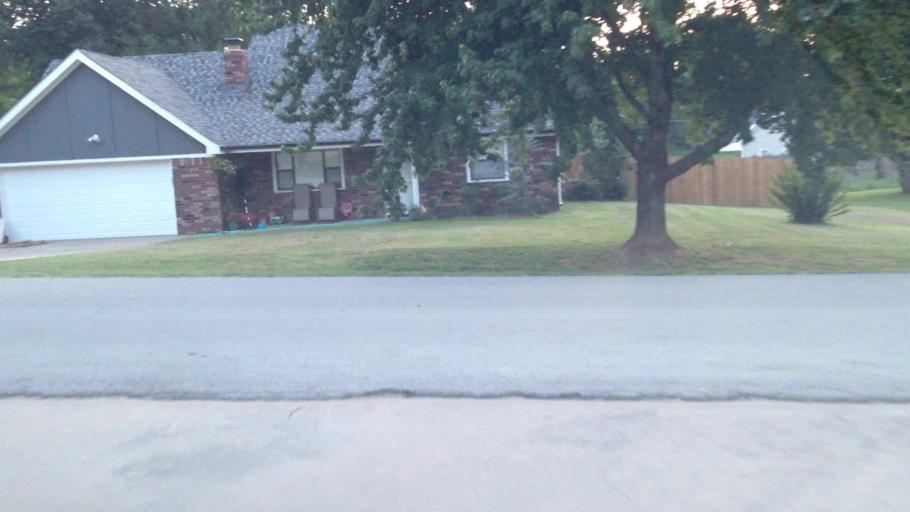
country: US
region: Kansas
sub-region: Montgomery County
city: Independence
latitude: 37.2522
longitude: -95.7085
